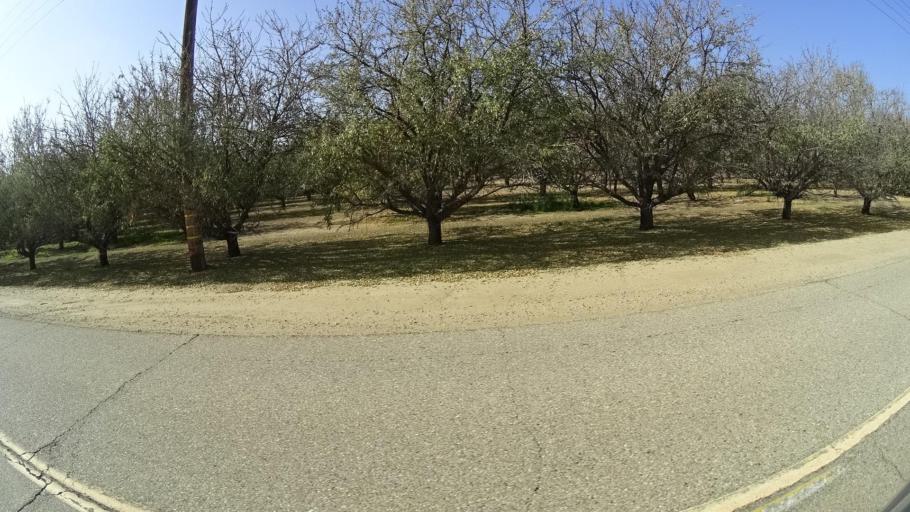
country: US
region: California
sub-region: Kern County
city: Rosedale
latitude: 35.4934
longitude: -119.1527
